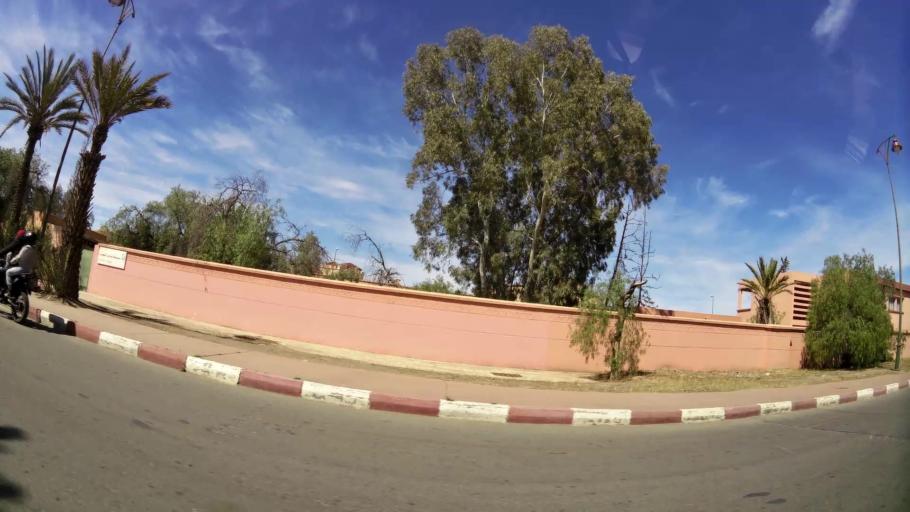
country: MA
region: Marrakech-Tensift-Al Haouz
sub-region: Marrakech
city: Marrakesh
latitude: 31.6503
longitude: -8.0570
